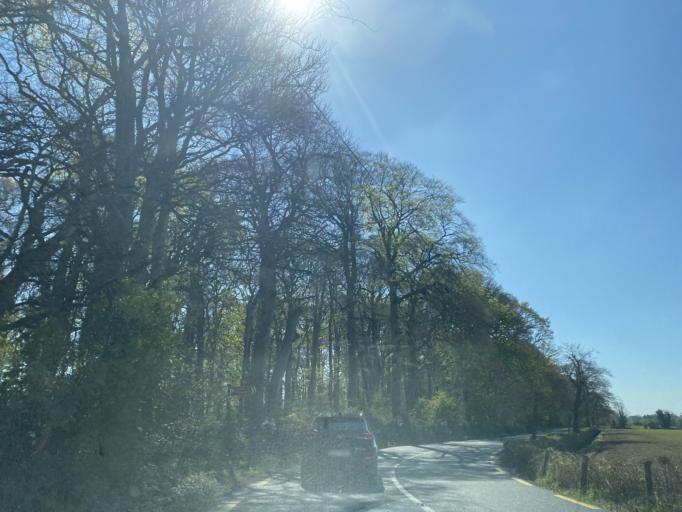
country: IE
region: Leinster
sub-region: Kildare
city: Kill
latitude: 53.2604
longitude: -6.5856
